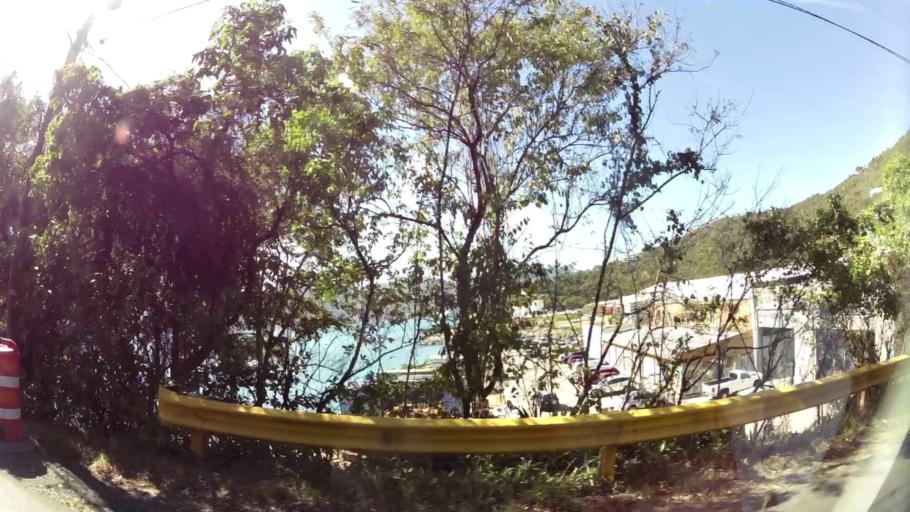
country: VG
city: Tortola
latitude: 18.4173
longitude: -64.5979
